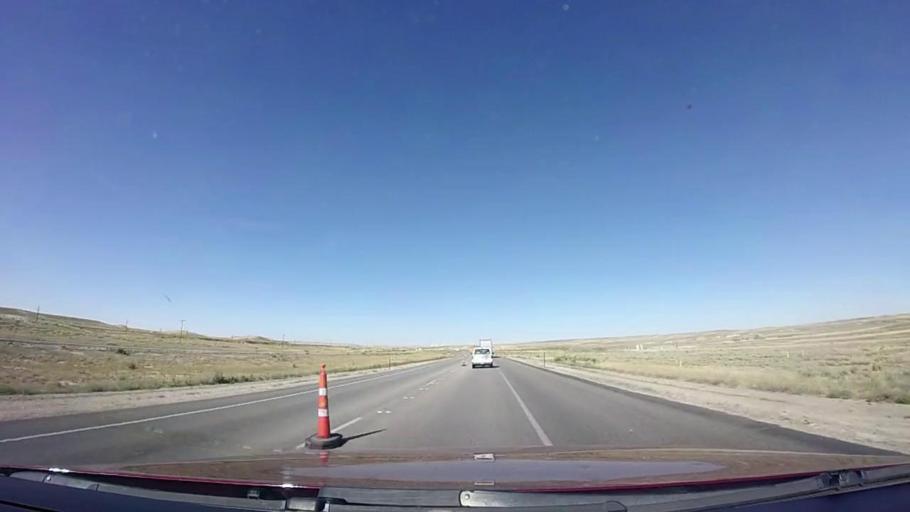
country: US
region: Wyoming
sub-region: Carbon County
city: Rawlins
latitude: 41.7052
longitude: -107.8916
